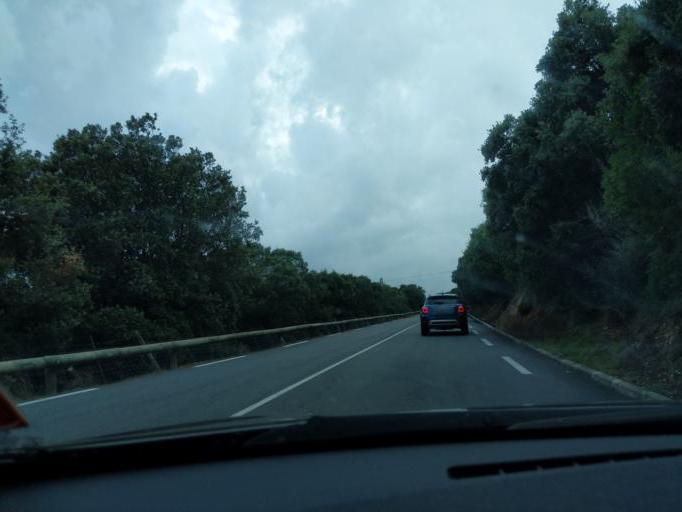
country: FR
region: Corsica
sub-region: Departement de la Corse-du-Sud
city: Sartene
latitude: 41.5796
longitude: 8.9450
